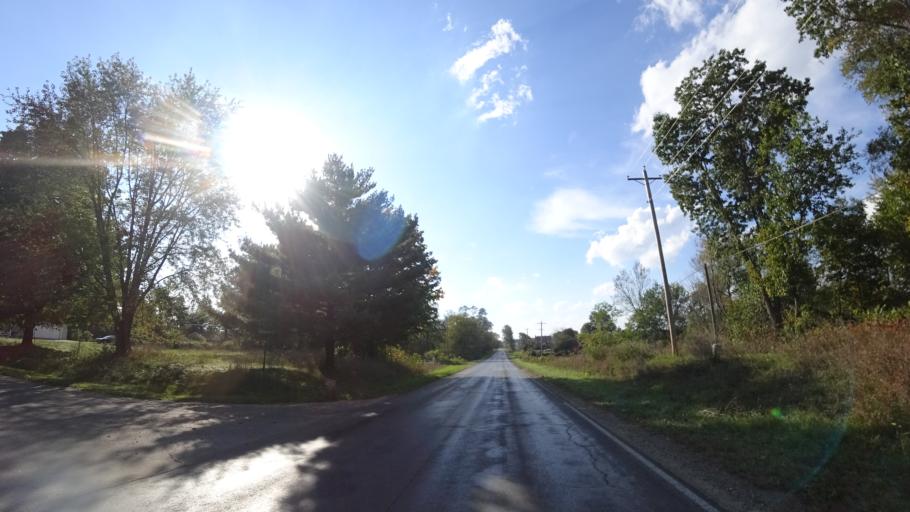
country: US
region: Michigan
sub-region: Saint Joseph County
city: Three Rivers
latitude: 41.9543
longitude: -85.6501
